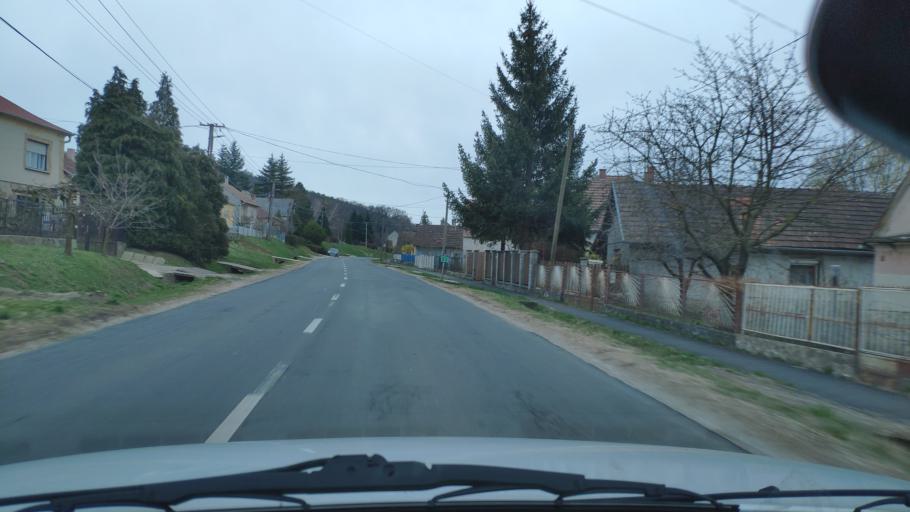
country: HU
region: Zala
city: Nagykanizsa
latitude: 46.5401
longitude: 16.9854
